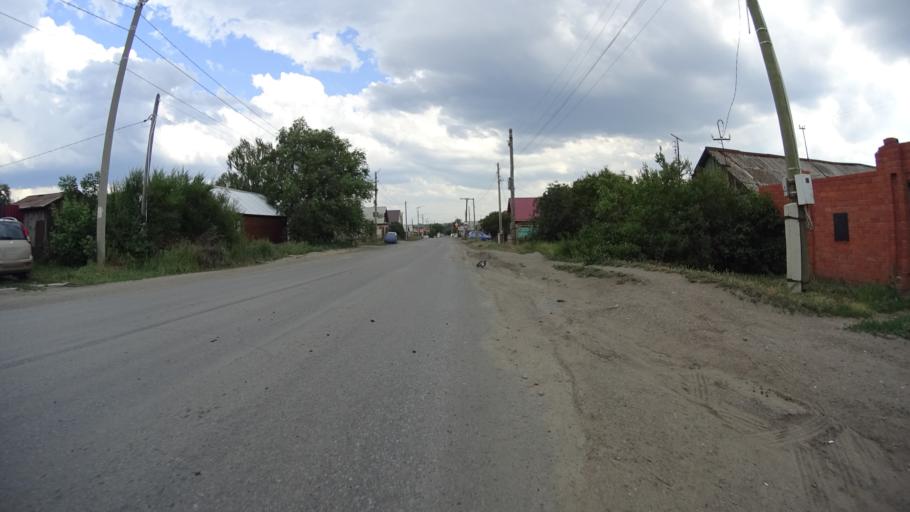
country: RU
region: Chelyabinsk
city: Troitsk
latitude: 54.0991
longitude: 61.5911
